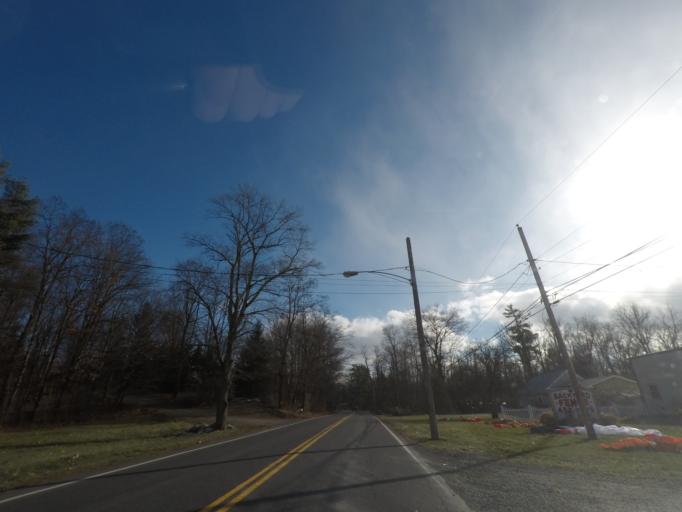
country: US
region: New York
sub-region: Albany County
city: Colonie
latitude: 42.7383
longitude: -73.8674
